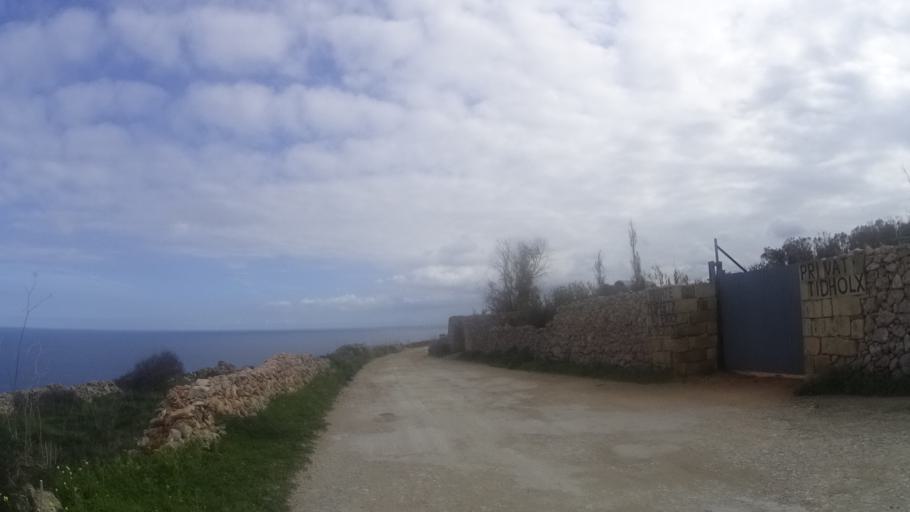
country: MT
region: Il-Qala
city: Qala
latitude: 36.0404
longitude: 14.3214
